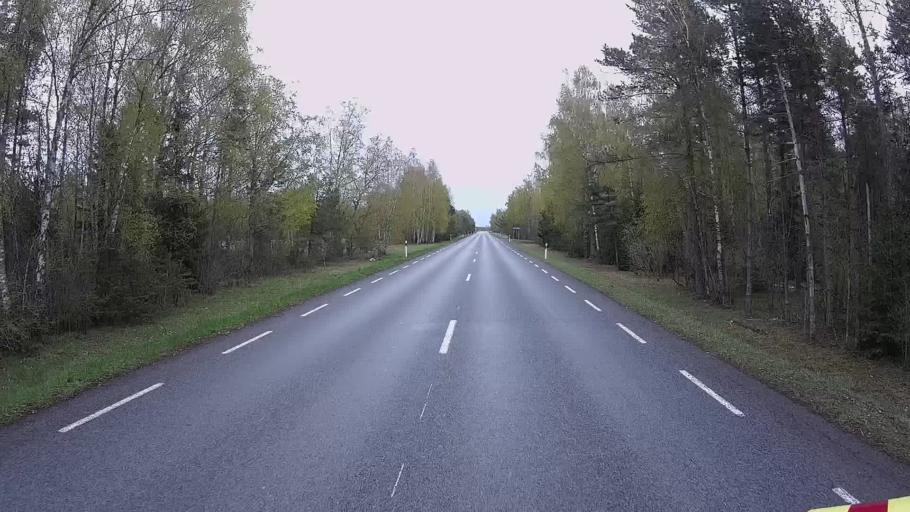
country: EE
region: Laeaene
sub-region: Vormsi vald
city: Hullo
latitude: 58.8663
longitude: 23.0230
